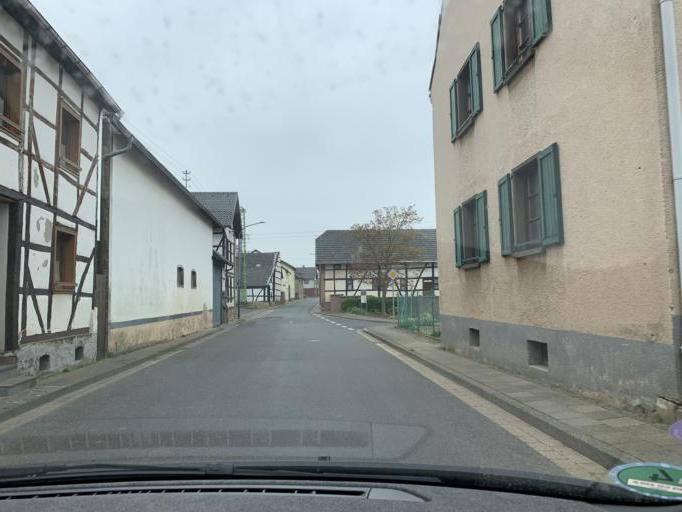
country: DE
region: North Rhine-Westphalia
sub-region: Regierungsbezirk Koln
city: Vettweiss
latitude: 50.6879
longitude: 6.5573
